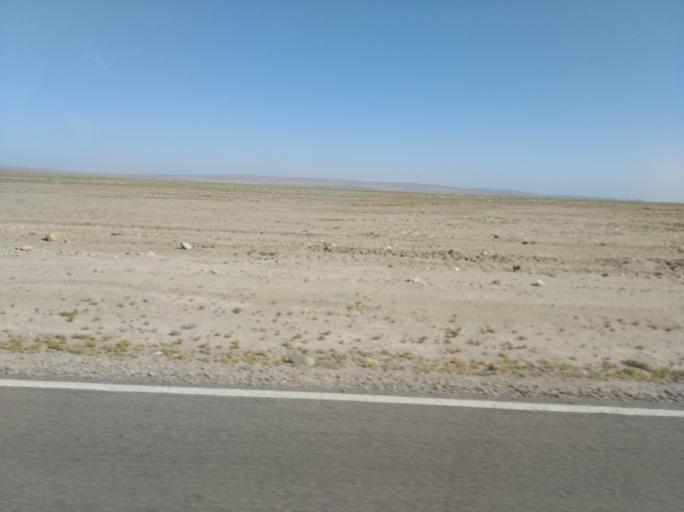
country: CL
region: Atacama
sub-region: Provincia de Copiapo
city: Copiapo
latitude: -27.3165
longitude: -70.8645
